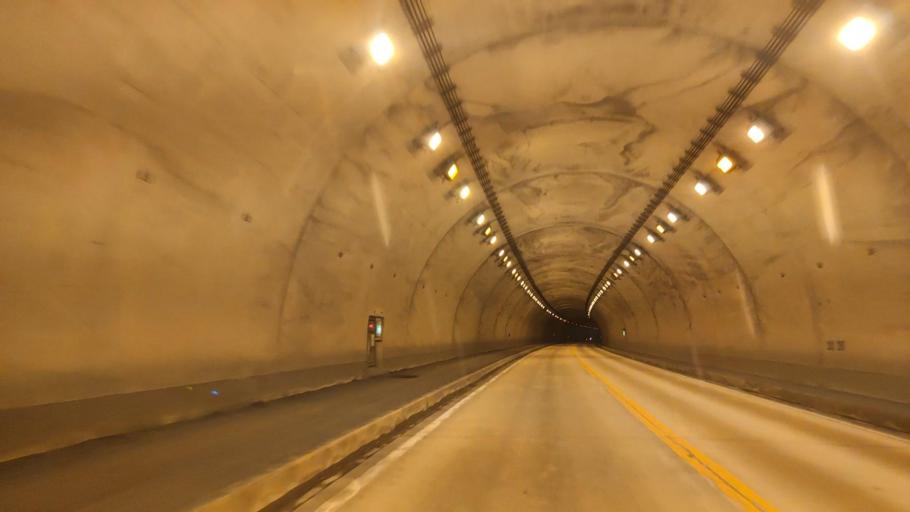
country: JP
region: Hyogo
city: Toyooka
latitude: 35.4594
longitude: 134.7685
